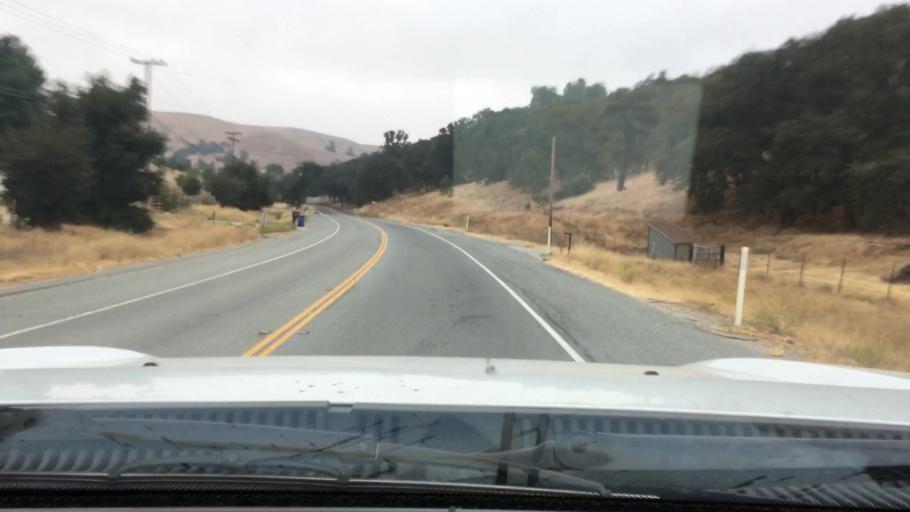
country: US
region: California
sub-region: San Luis Obispo County
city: Atascadero
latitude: 35.5059
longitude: -120.6471
